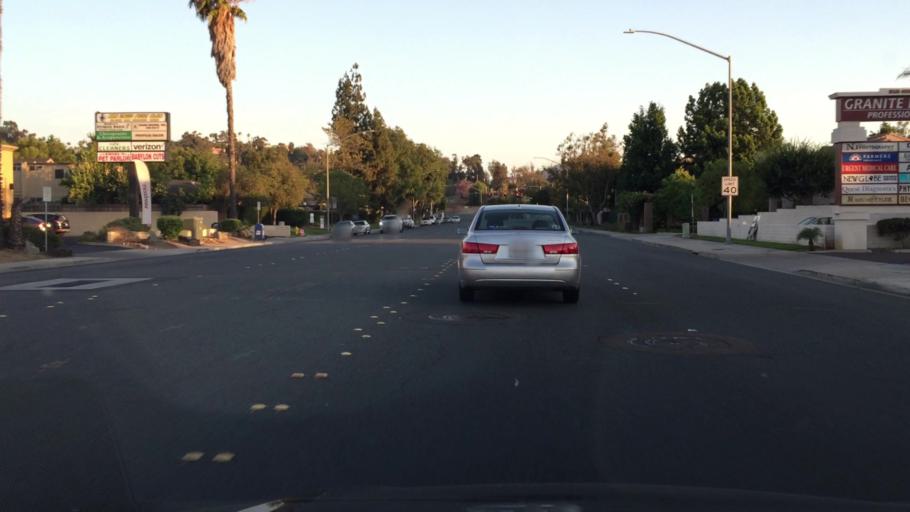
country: US
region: California
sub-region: San Diego County
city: Bostonia
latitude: 32.7847
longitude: -116.9280
